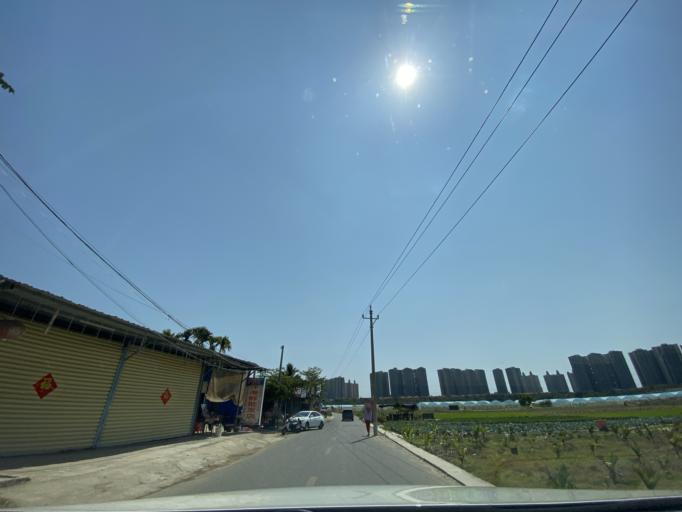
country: CN
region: Hainan
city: Yingzhou
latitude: 18.4212
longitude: 109.8774
